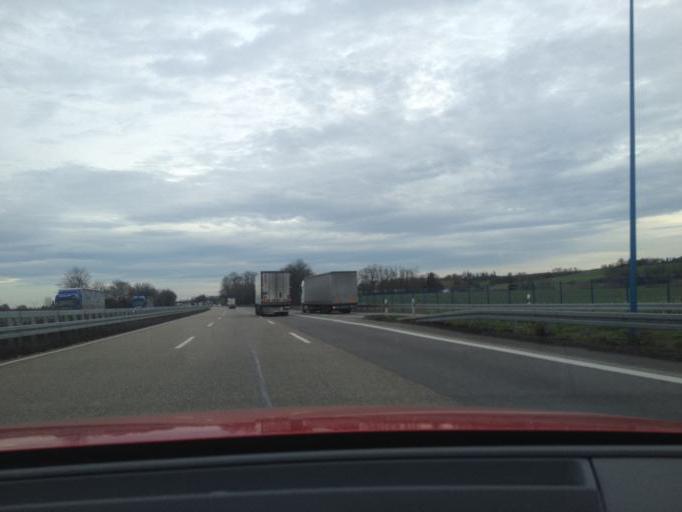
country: DE
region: Baden-Wuerttemberg
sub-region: Regierungsbezirk Stuttgart
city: Waldenburg
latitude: 49.2058
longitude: 9.6417
